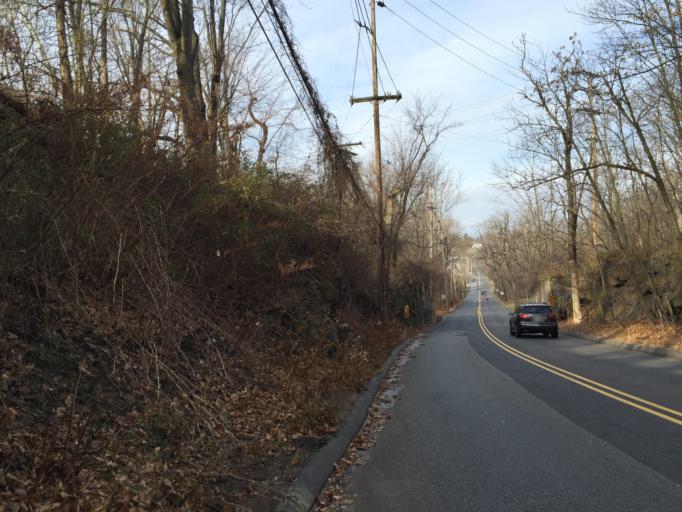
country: US
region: New Jersey
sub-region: Union County
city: Springfield
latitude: 40.7112
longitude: -74.3359
